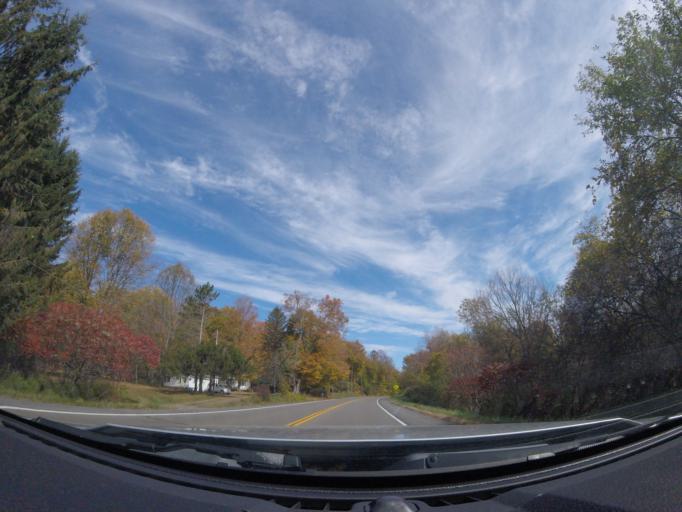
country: US
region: New York
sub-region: Cortland County
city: Cortland West
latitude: 42.5682
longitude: -76.2578
